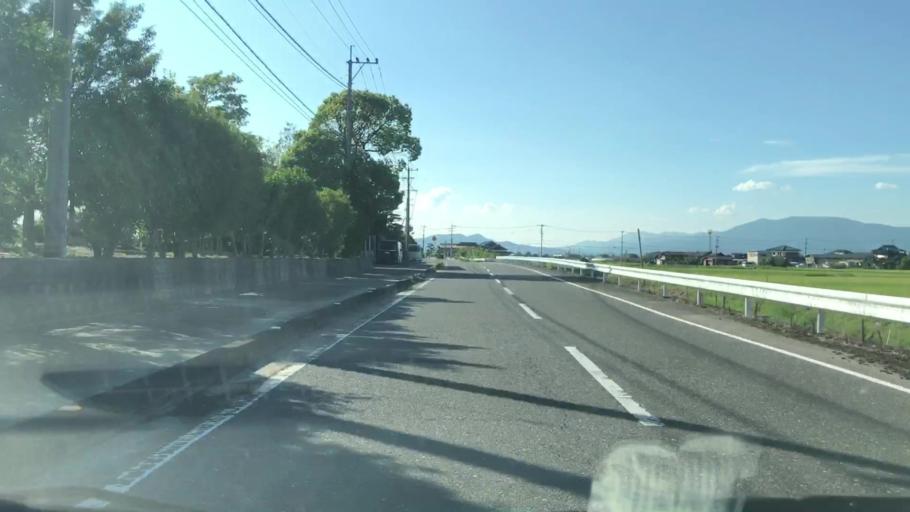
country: JP
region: Saga Prefecture
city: Saga-shi
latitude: 33.1915
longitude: 130.2809
